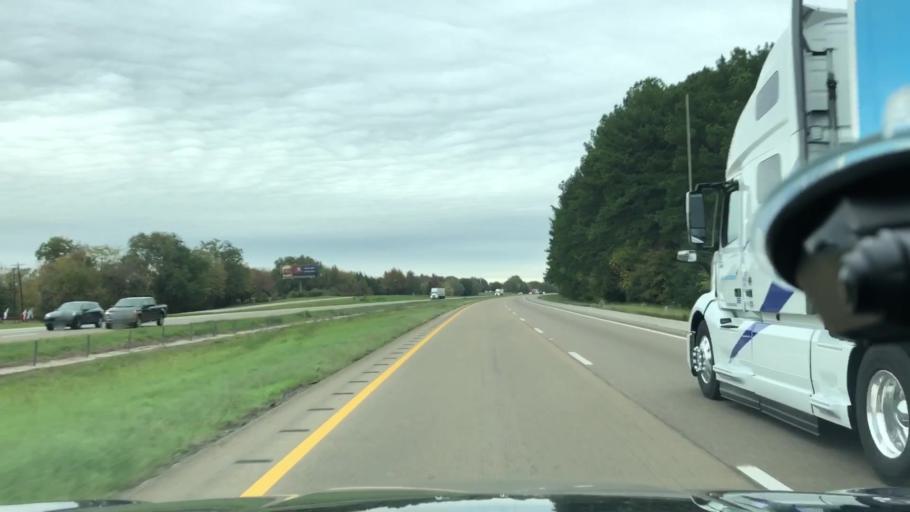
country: US
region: Texas
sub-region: Titus County
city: Mount Pleasant
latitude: 33.2268
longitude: -94.8876
